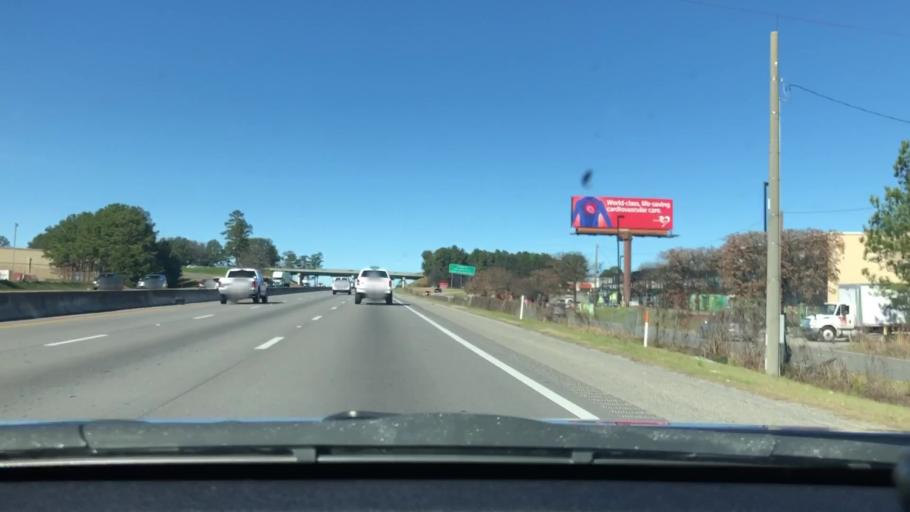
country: US
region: South Carolina
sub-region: Lexington County
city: Seven Oaks
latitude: 34.0749
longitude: -81.1495
